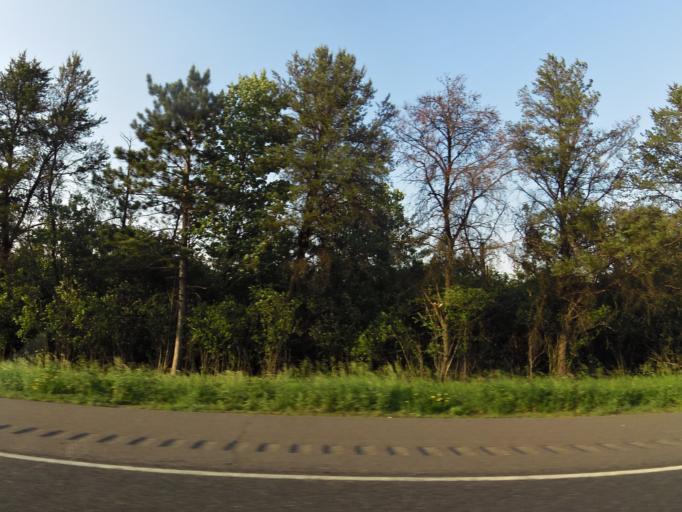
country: US
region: Wisconsin
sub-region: Jackson County
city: Black River Falls
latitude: 44.2782
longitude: -90.8039
